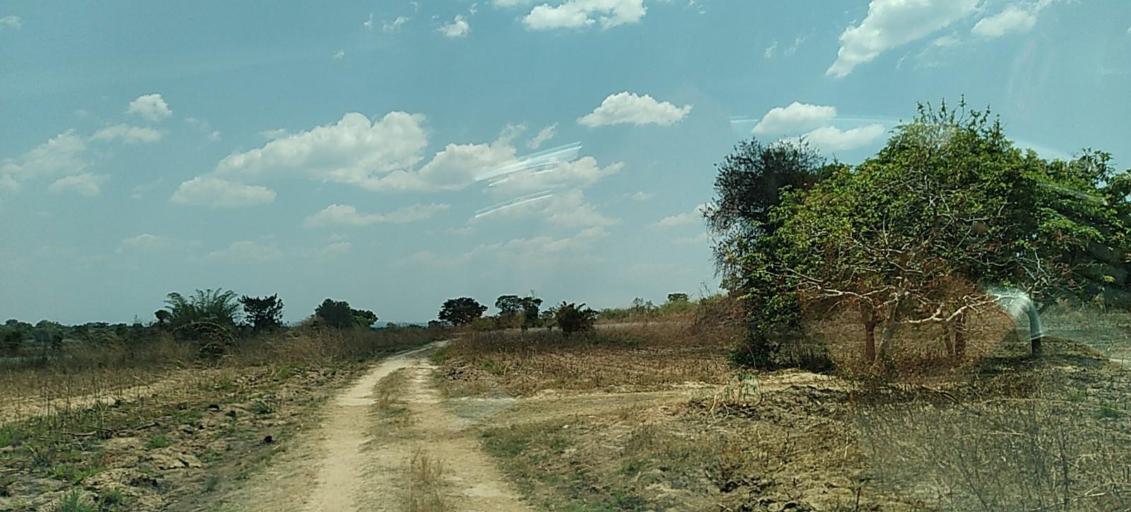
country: ZM
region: Copperbelt
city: Chililabombwe
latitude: -12.4694
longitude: 27.6659
